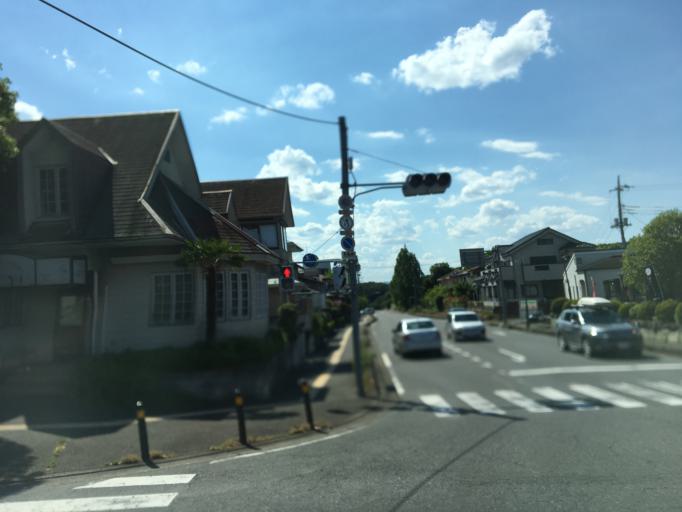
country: JP
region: Saitama
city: Sakado
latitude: 35.9915
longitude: 139.3544
